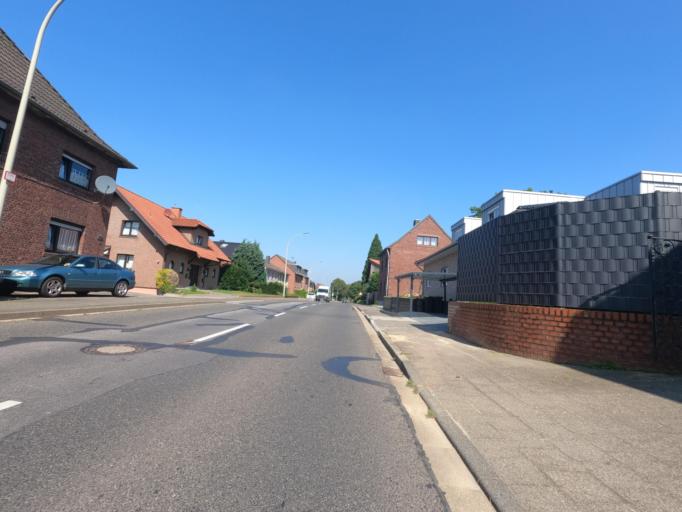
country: DE
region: North Rhine-Westphalia
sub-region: Regierungsbezirk Koln
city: Ubach-Palenberg
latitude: 50.9472
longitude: 6.1065
